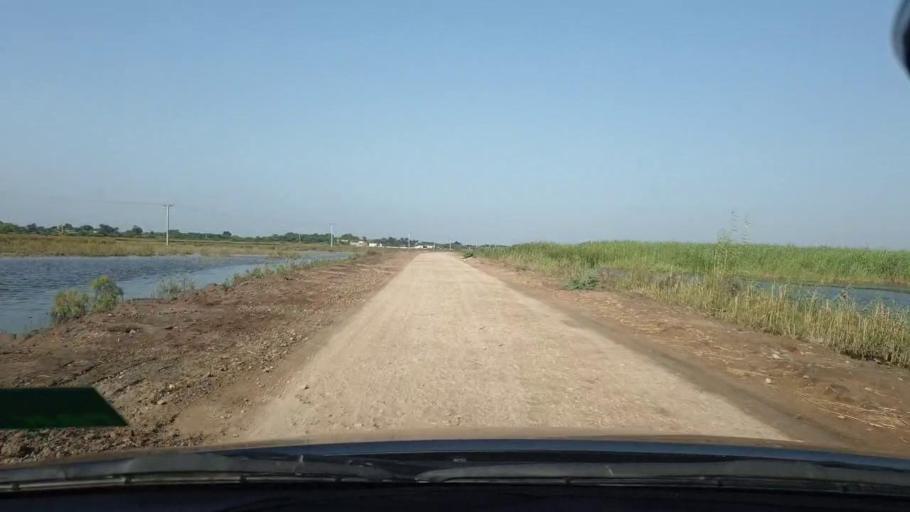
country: PK
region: Sindh
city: Tando Bago
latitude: 24.7229
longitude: 68.9500
